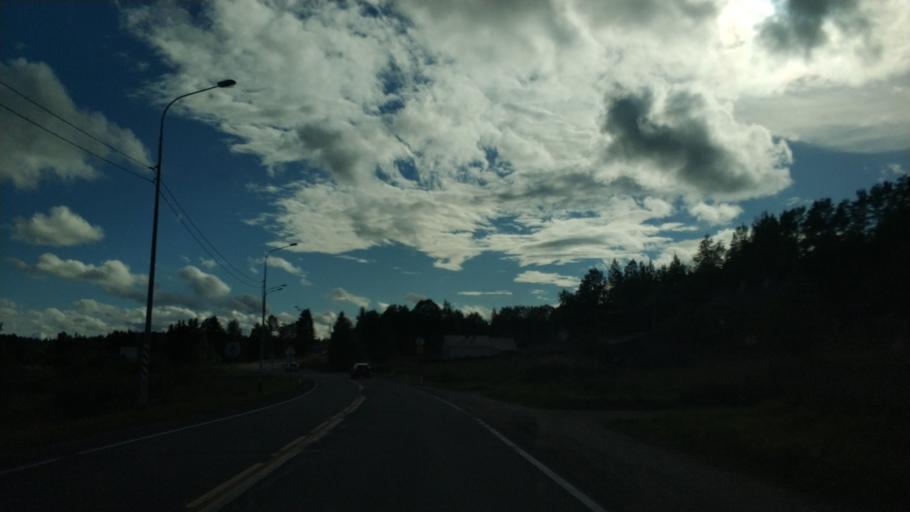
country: RU
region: Republic of Karelia
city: Lakhdenpokh'ya
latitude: 61.5549
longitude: 30.3226
